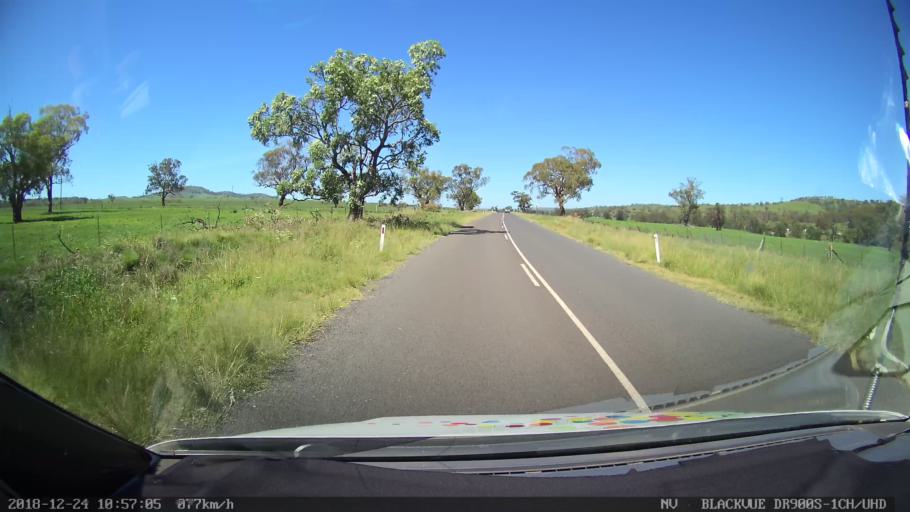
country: AU
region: New South Wales
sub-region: Upper Hunter Shire
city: Merriwa
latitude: -32.0325
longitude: 150.4158
